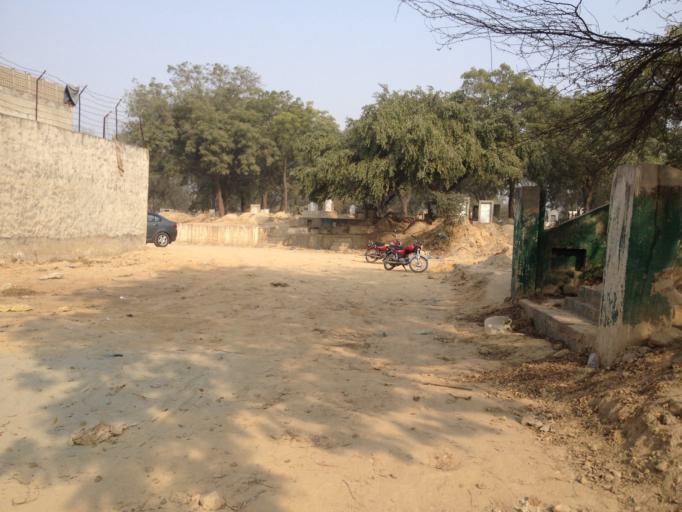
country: PK
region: Punjab
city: Lahore
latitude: 31.5770
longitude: 74.4153
